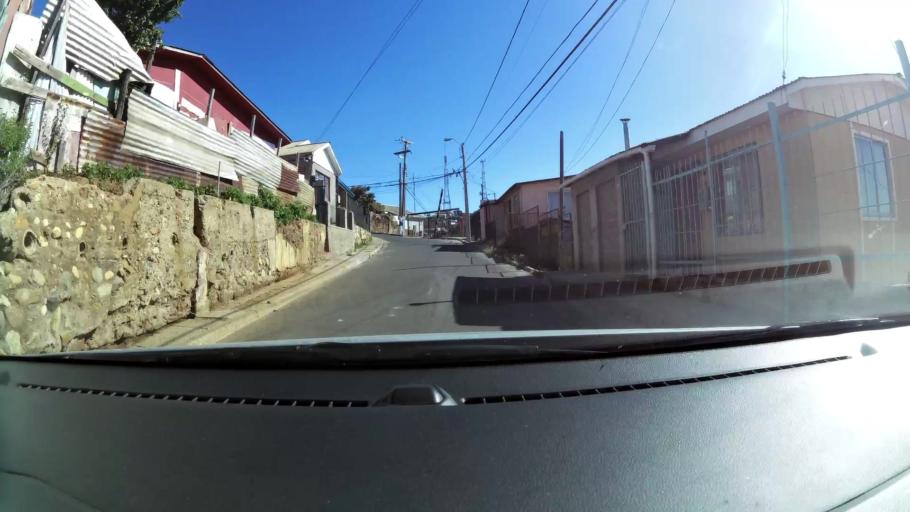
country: CL
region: Valparaiso
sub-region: Provincia de Valparaiso
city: Vina del Mar
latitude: -33.0450
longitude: -71.5601
